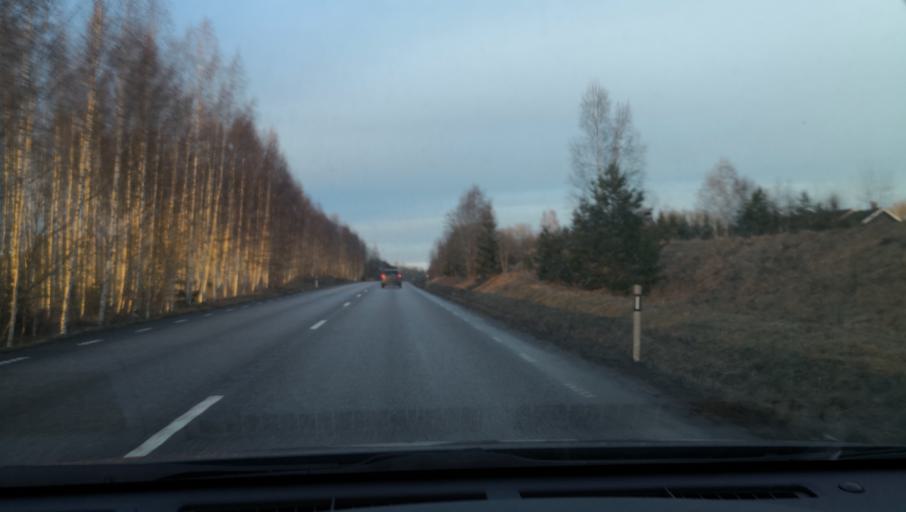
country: SE
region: OErebro
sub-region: Lekebergs Kommun
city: Fjugesta
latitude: 59.1784
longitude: 14.8576
